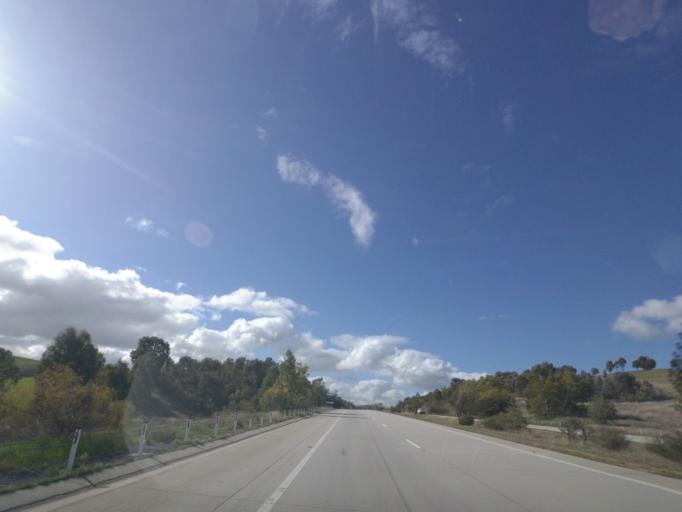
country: AU
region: New South Wales
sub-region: Albury Municipality
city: Lavington
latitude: -35.9213
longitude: 147.0941
